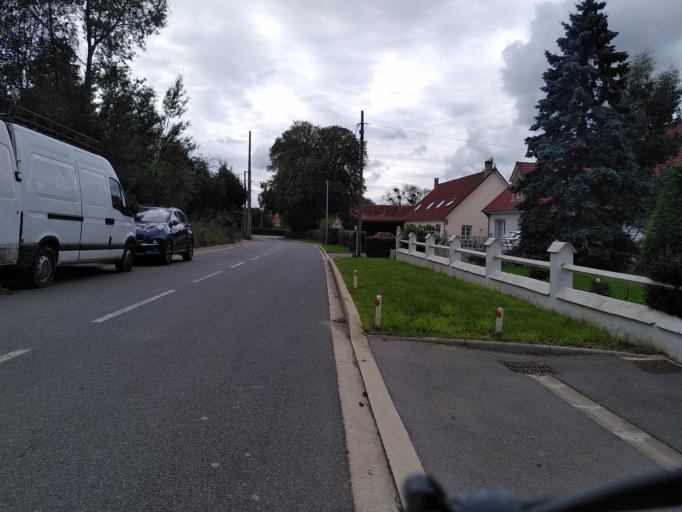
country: FR
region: Nord-Pas-de-Calais
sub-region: Departement du Pas-de-Calais
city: Longfosse
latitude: 50.6930
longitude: 1.7869
